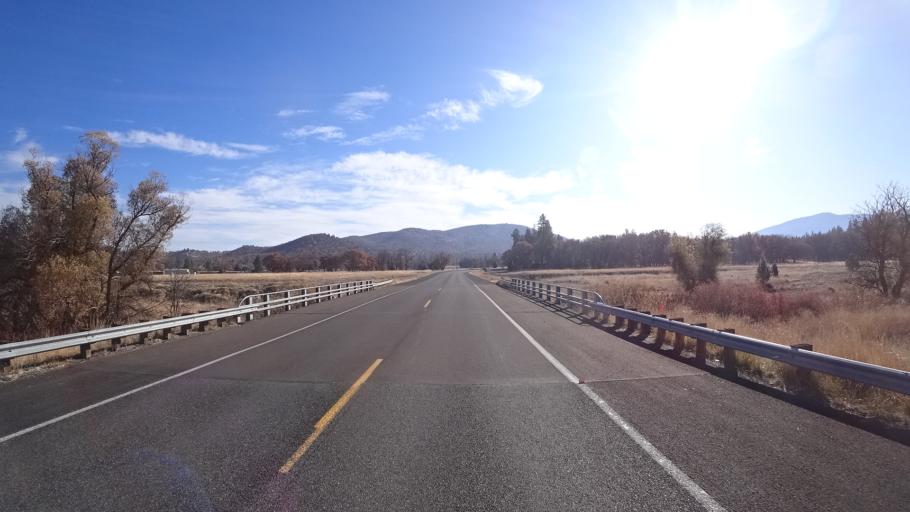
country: US
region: California
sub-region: Siskiyou County
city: Yreka
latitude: 41.6955
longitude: -122.6440
